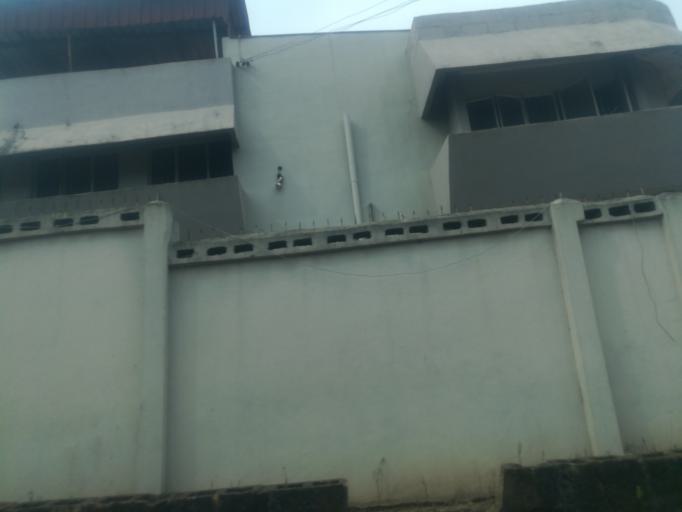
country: NG
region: Oyo
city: Ibadan
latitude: 7.4145
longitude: 3.8970
